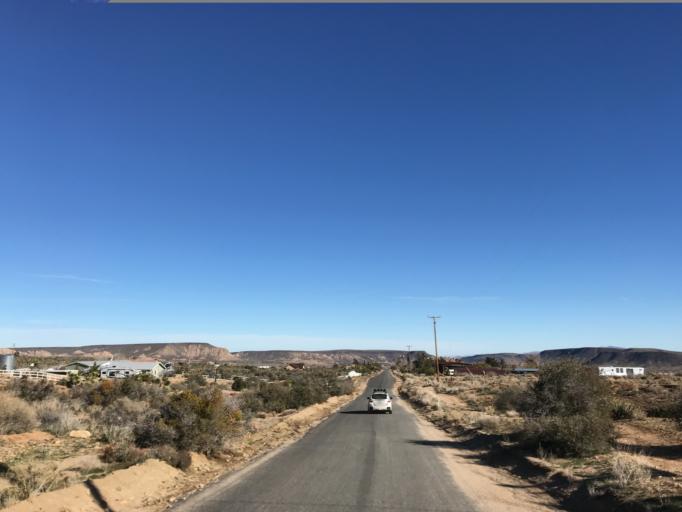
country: US
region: California
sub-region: San Bernardino County
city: Yucca Valley
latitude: 34.1980
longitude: -116.5584
